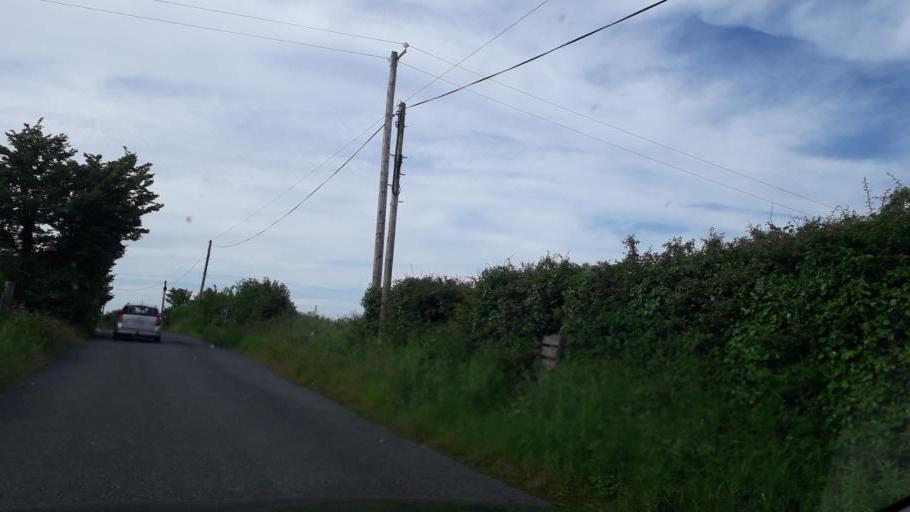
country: IE
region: Leinster
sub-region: Loch Garman
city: Courtown
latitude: 52.5350
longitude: -6.2554
